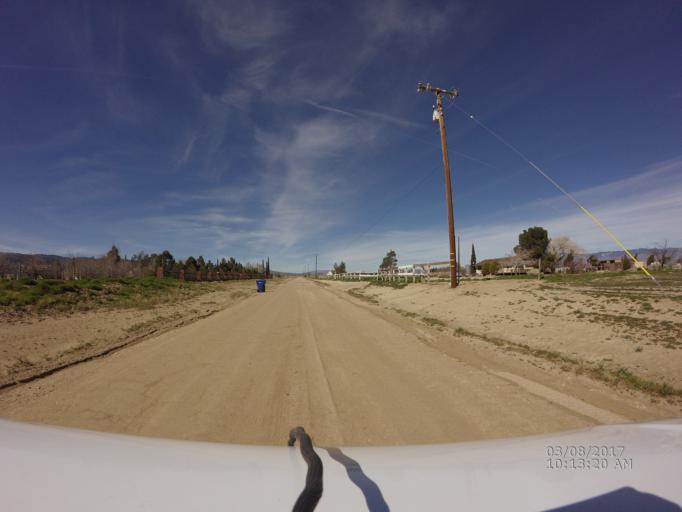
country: US
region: California
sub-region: Los Angeles County
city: Green Valley
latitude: 34.7530
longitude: -118.4608
